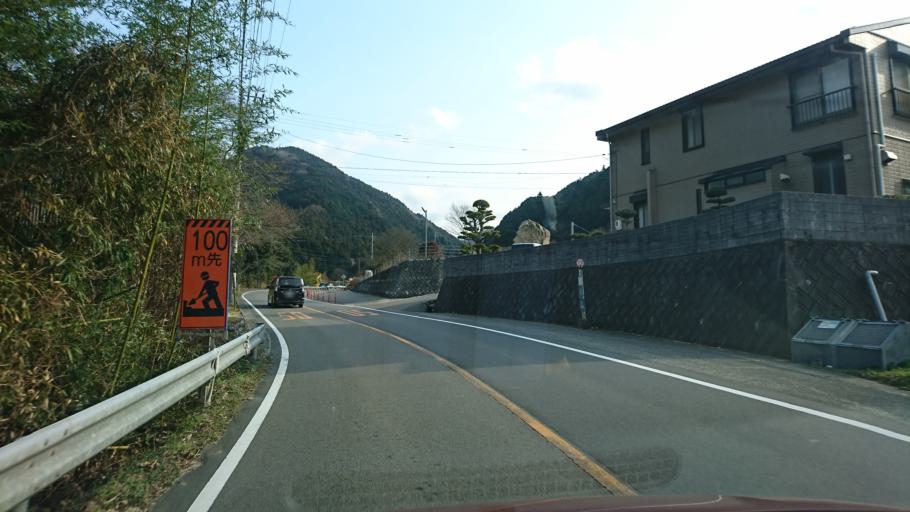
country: JP
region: Ehime
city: Hojo
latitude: 33.9694
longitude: 132.9032
